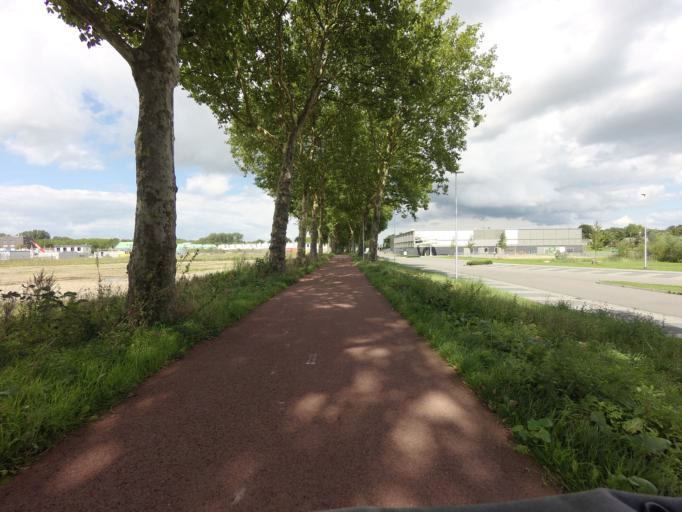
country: NL
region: Utrecht
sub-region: Gemeente Vianen
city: Vianen
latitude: 51.9850
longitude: 5.0814
